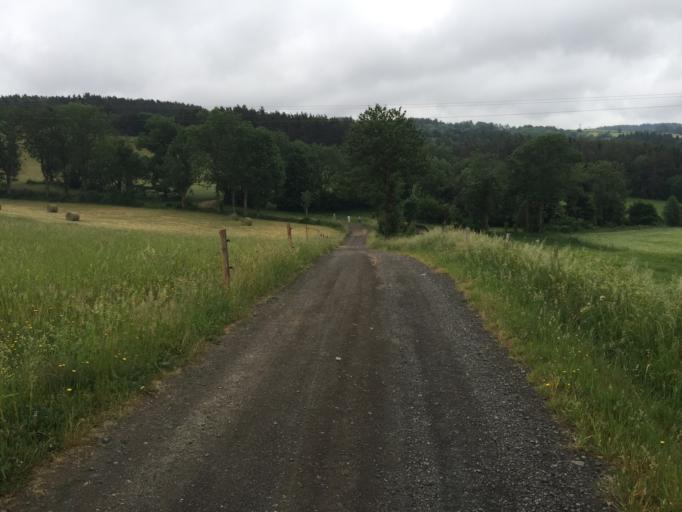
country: FR
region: Auvergne
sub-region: Departement de la Haute-Loire
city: Yssingeaux
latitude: 45.1369
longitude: 4.1558
